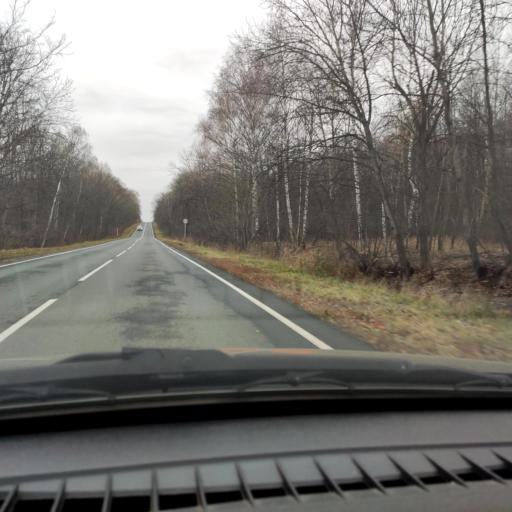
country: RU
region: Samara
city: Zhigulevsk
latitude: 53.3441
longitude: 49.5488
